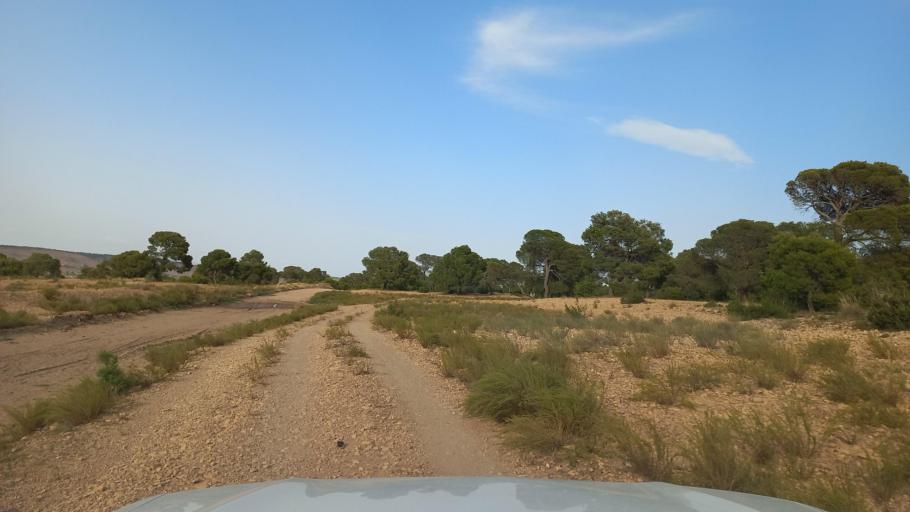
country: TN
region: Al Qasrayn
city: Kasserine
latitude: 35.3351
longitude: 8.8527
